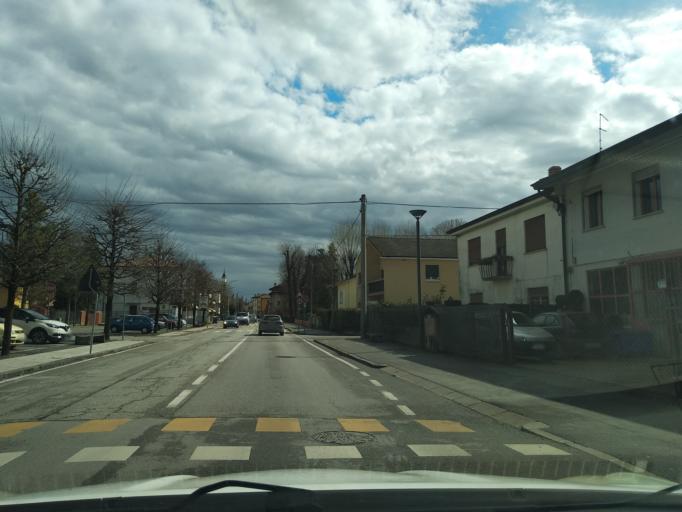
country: IT
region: Veneto
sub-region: Provincia di Vicenza
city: Monticello Conte Otto
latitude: 45.5949
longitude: 11.5809
